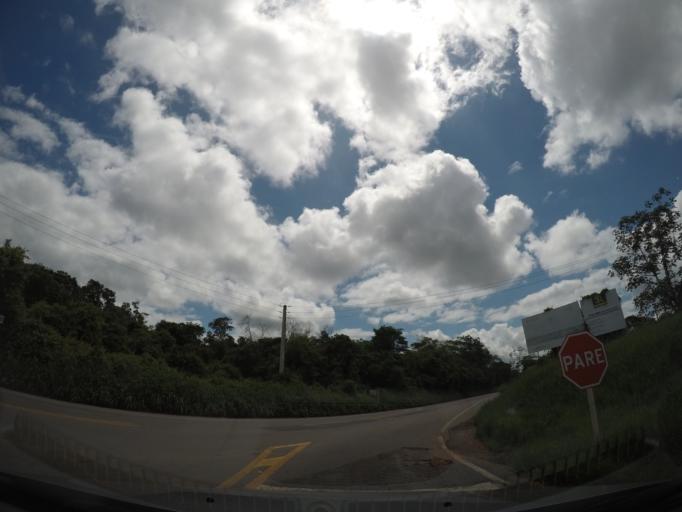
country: BR
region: Bahia
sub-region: Iraquara
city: Iraquara
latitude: -12.4781
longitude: -41.3594
